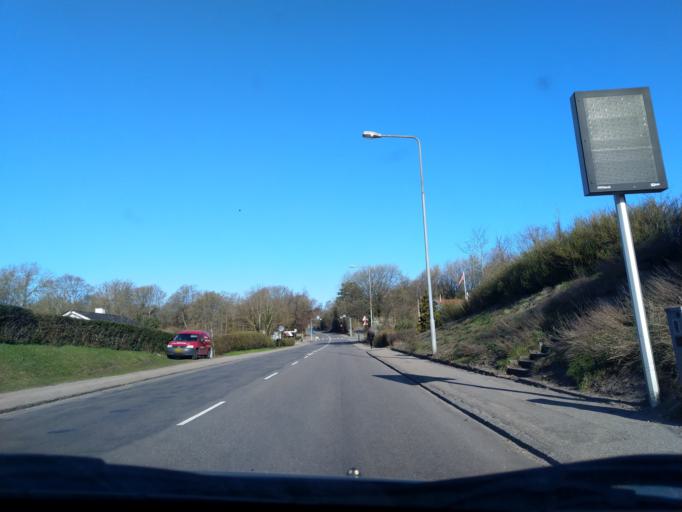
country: DK
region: Zealand
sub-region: Kalundborg Kommune
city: Kalundborg
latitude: 55.6980
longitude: 11.0401
